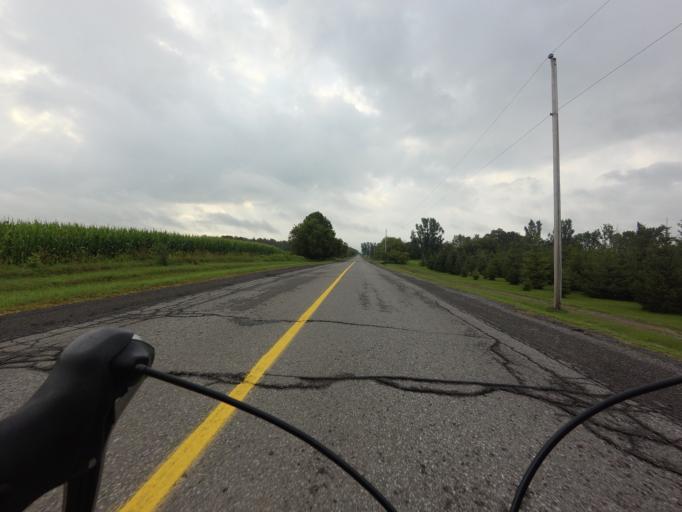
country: CA
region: Ontario
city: Bells Corners
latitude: 45.1287
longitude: -75.7838
